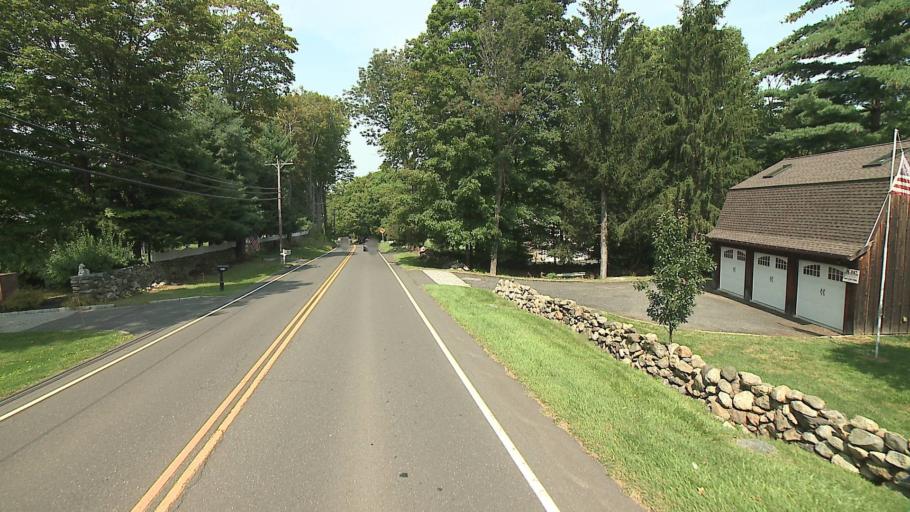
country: US
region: Connecticut
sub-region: Fairfield County
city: Ridgefield
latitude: 41.3215
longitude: -73.5203
